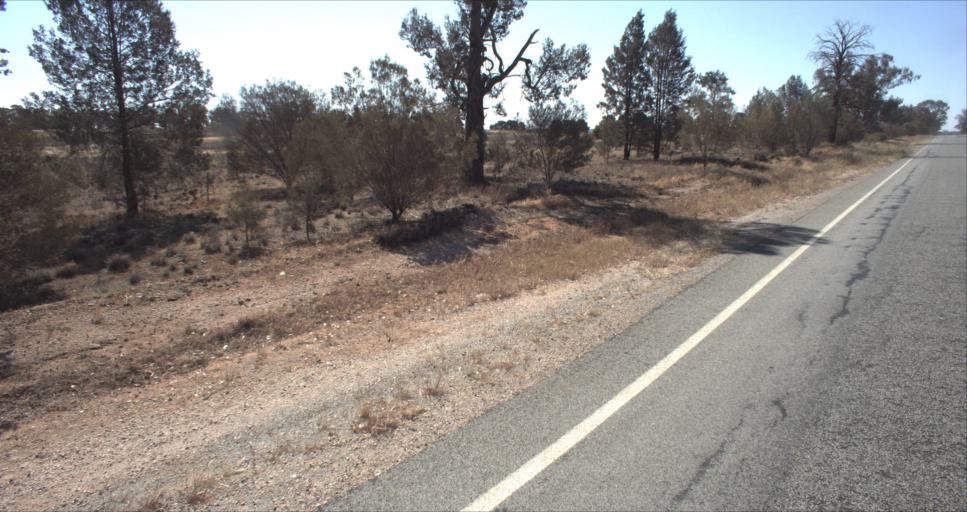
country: AU
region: New South Wales
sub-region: Leeton
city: Leeton
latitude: -34.4823
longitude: 146.4340
